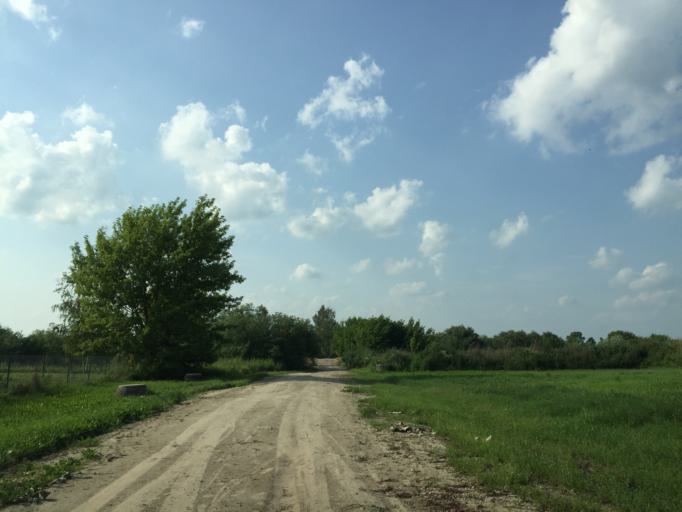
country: LV
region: Jelgava
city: Jelgava
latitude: 56.6666
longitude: 23.7141
